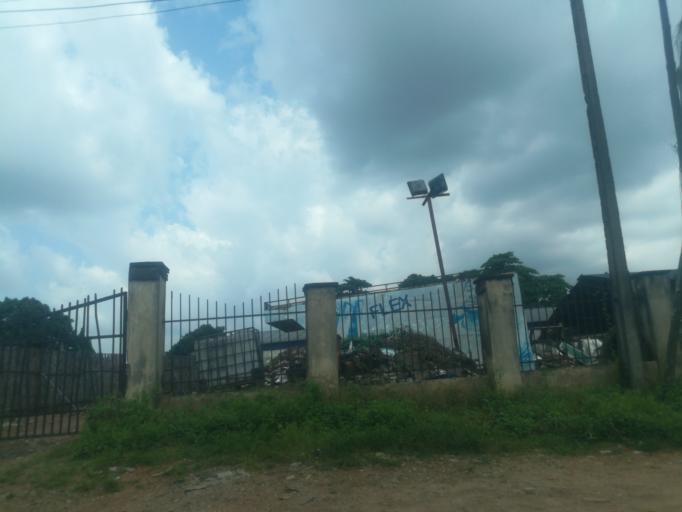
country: NG
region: Oyo
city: Ibadan
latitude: 7.3610
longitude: 3.8525
